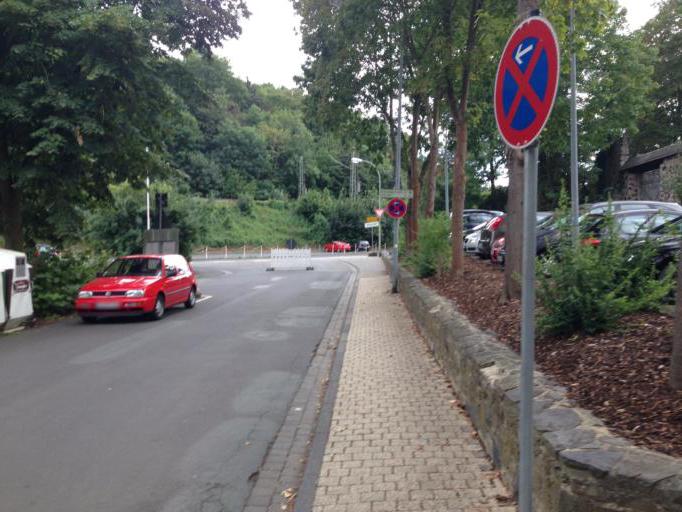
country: DE
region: Hesse
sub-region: Regierungsbezirk Giessen
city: Limburg an der Lahn
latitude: 50.3876
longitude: 8.0689
